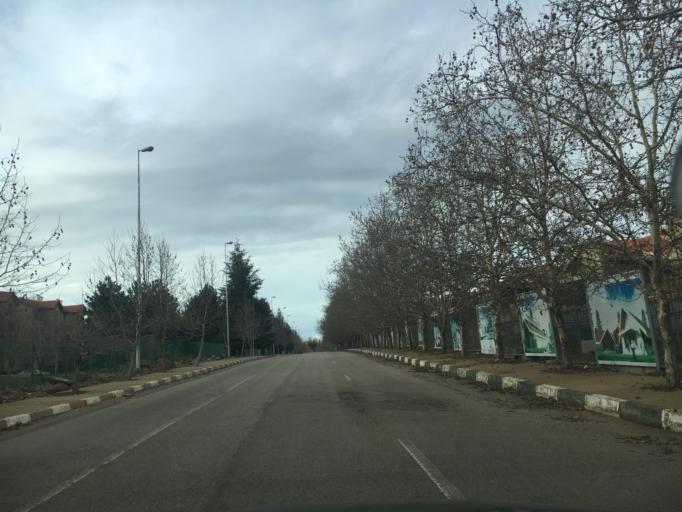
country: MA
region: Meknes-Tafilalet
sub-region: Ifrane
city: Ifrane
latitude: 33.5253
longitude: -5.1329
